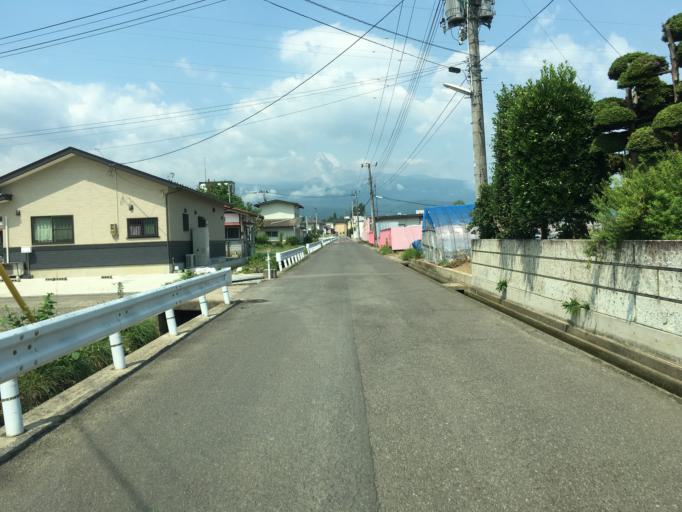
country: JP
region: Fukushima
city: Fukushima-shi
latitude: 37.7393
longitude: 140.4291
